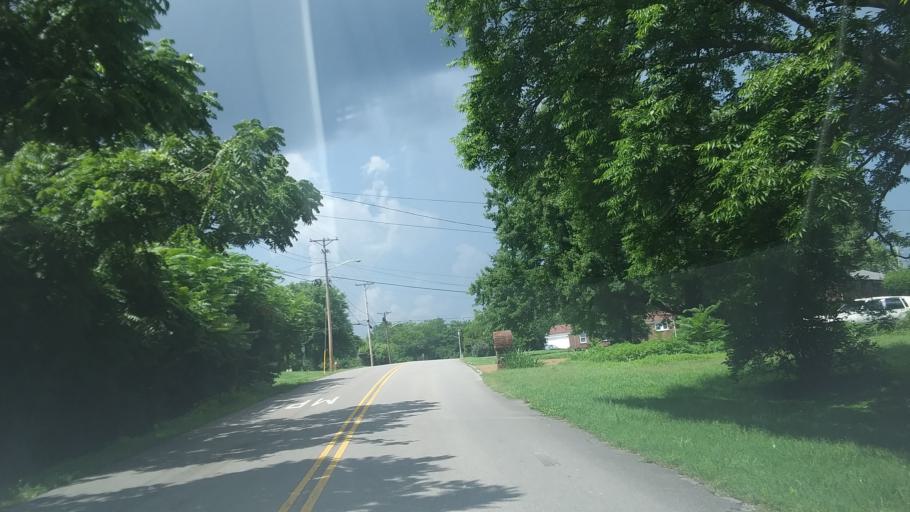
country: US
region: Tennessee
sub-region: Davidson County
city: Oak Hill
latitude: 36.0719
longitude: -86.7162
